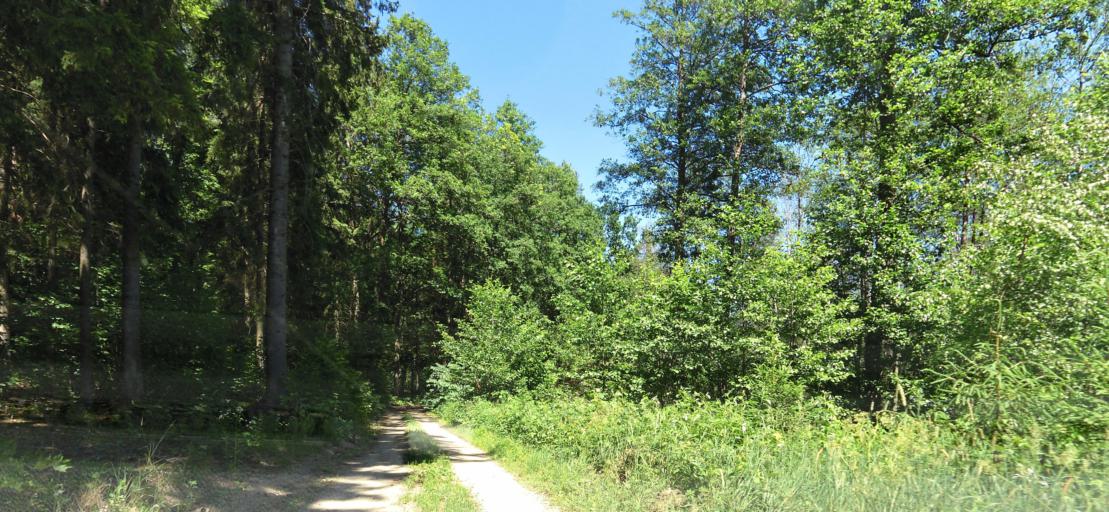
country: LT
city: Grigiskes
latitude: 54.8084
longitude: 25.0043
